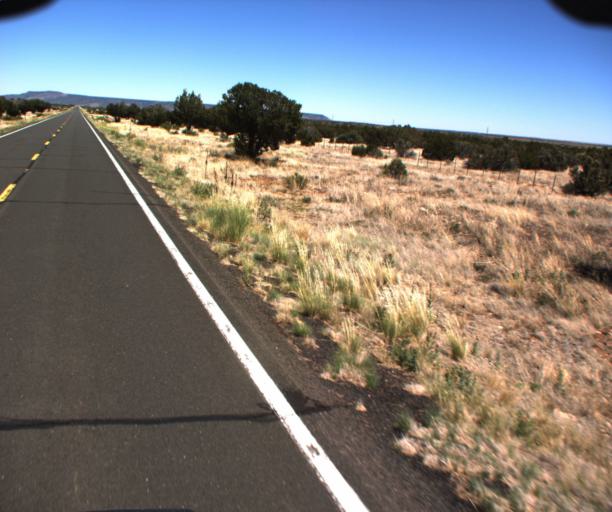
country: US
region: Arizona
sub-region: Coconino County
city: LeChee
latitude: 34.7500
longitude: -111.0397
